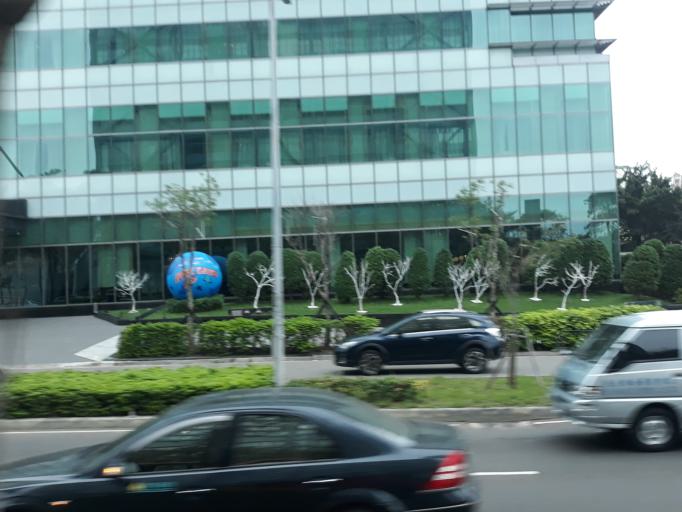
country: TW
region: Taiwan
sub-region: Hsinchu
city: Hsinchu
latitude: 24.7991
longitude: 121.0055
